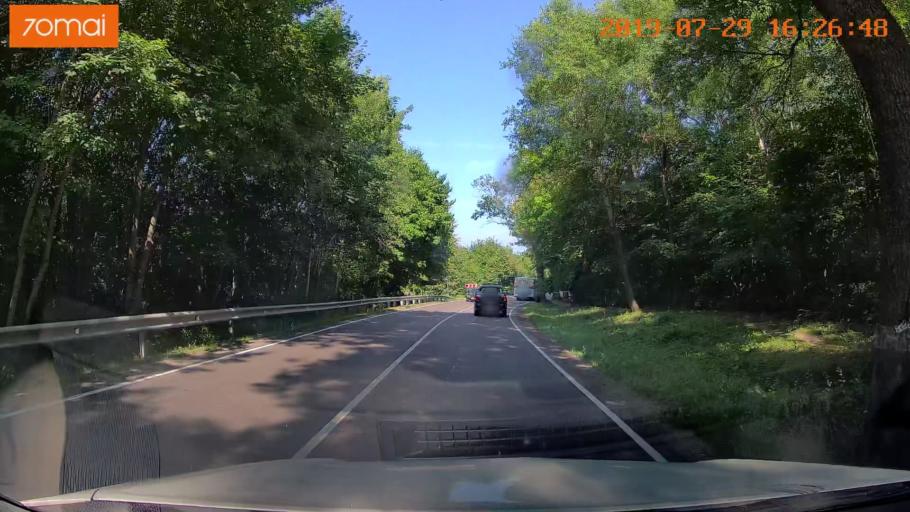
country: RU
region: Kaliningrad
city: Primorsk
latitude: 54.7300
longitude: 19.9832
